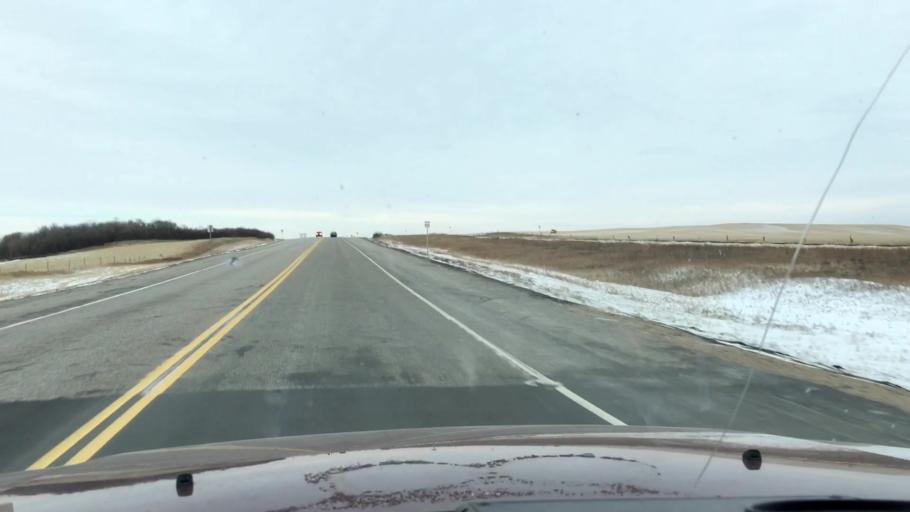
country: CA
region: Saskatchewan
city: Moose Jaw
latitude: 50.8472
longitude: -105.5602
